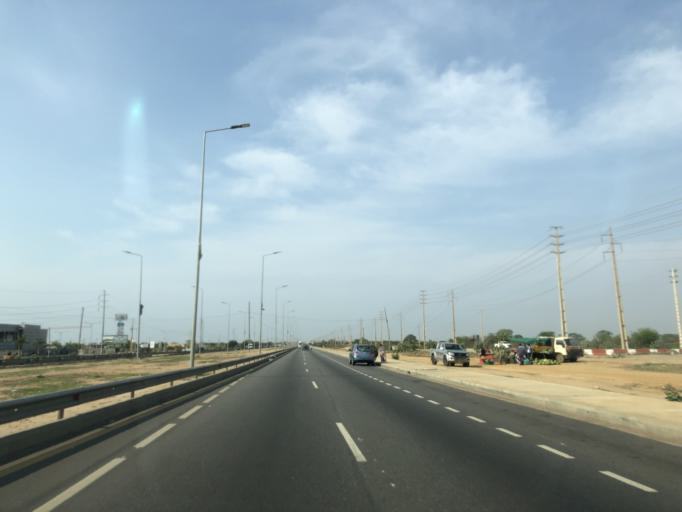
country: AO
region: Luanda
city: Luanda
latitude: -8.9563
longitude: 13.2581
